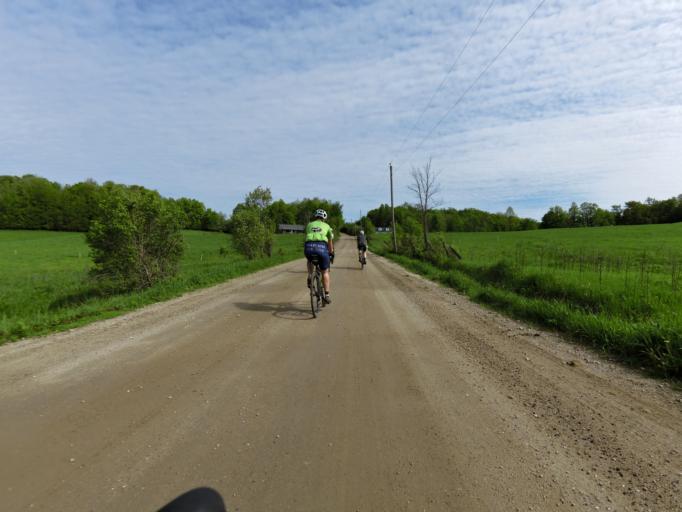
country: CA
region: Quebec
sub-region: Outaouais
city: Wakefield
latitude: 45.6999
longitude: -75.8958
